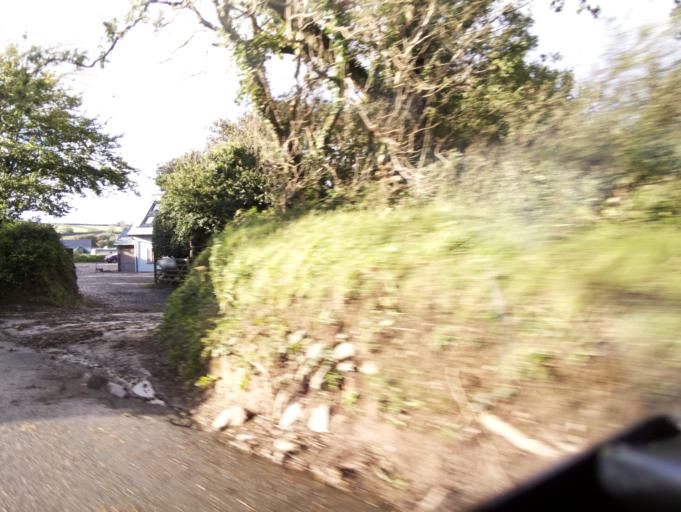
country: GB
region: England
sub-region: Devon
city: Totnes
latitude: 50.3596
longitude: -3.7319
